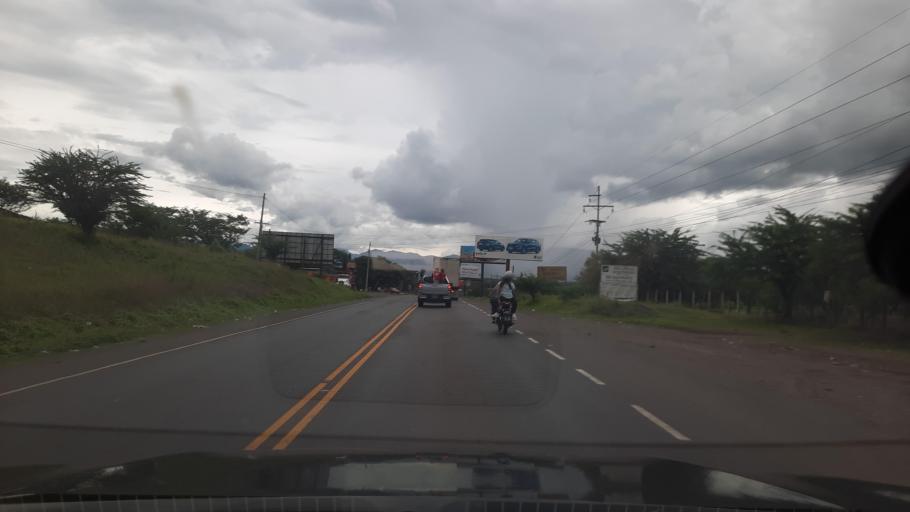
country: HN
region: Choluteca
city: Ciudad Choluteca
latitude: 13.3241
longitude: -87.2160
